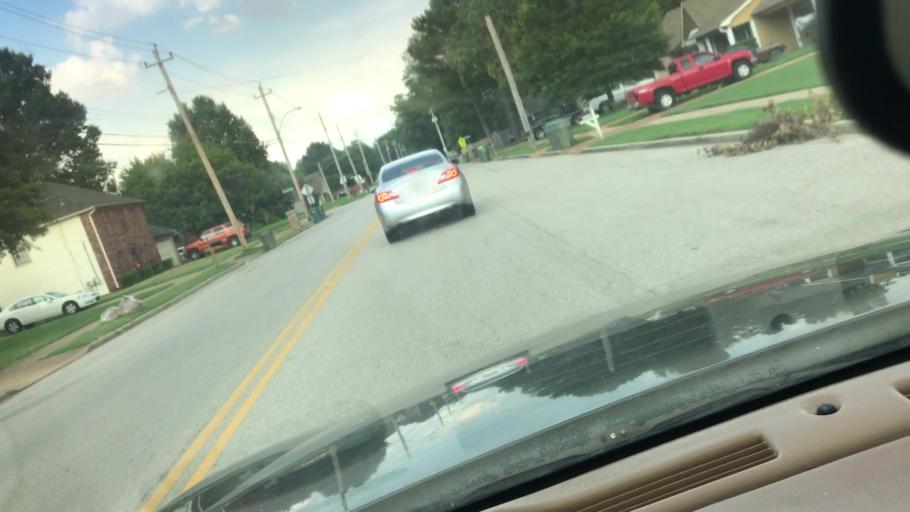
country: US
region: Tennessee
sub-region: Shelby County
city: Bartlett
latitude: 35.1939
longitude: -89.8086
